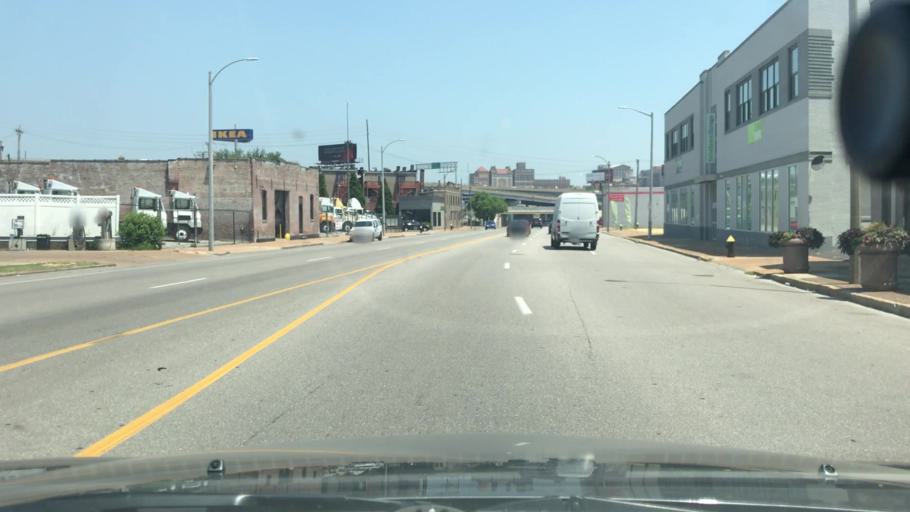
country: US
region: Missouri
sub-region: City of Saint Louis
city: St. Louis
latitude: 38.6299
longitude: -90.2456
